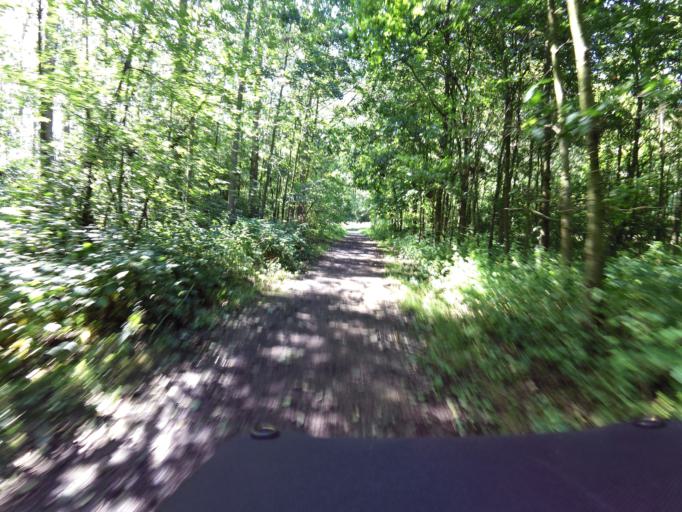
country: NL
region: South Holland
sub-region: Gemeente Goeree-Overflakkee
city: Dirksland
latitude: 51.7663
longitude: 4.0651
